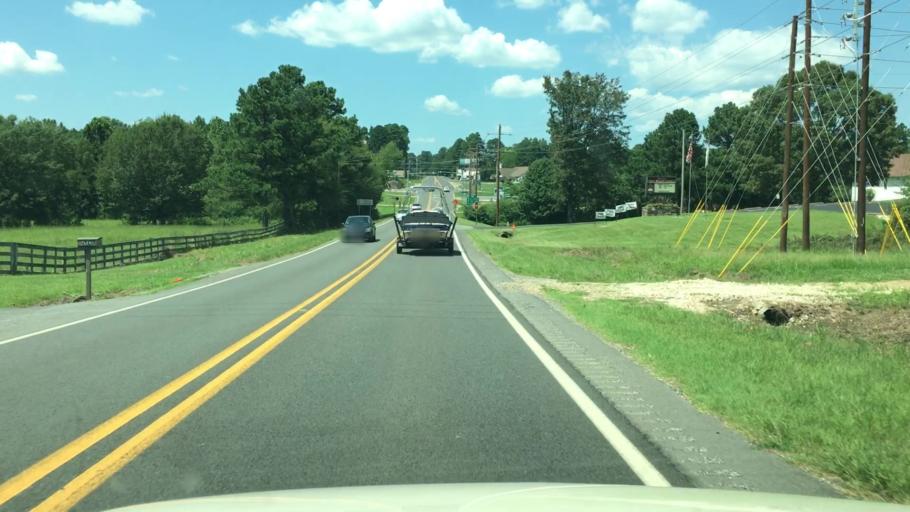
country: US
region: Arkansas
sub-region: Garland County
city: Lake Hamilton
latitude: 34.3137
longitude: -93.1699
